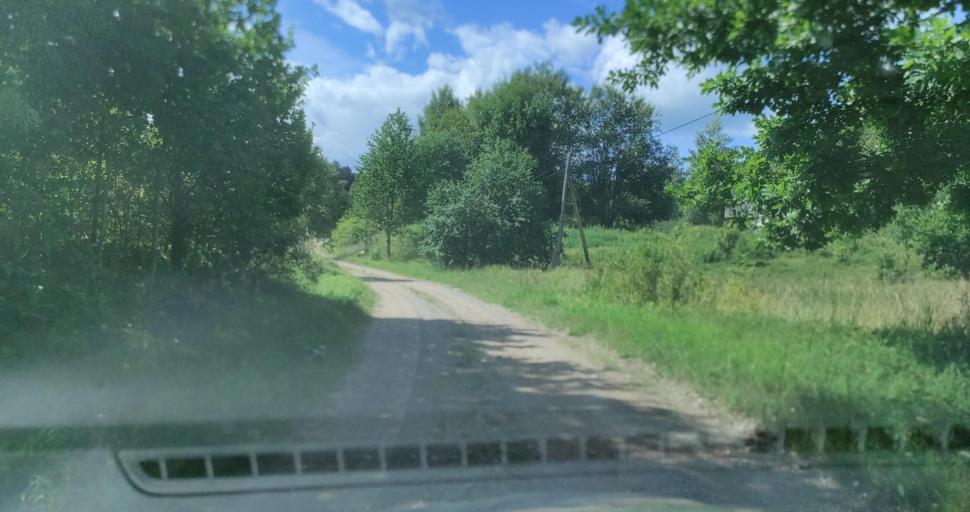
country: LV
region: Alsunga
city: Alsunga
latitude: 57.0276
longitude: 21.6973
